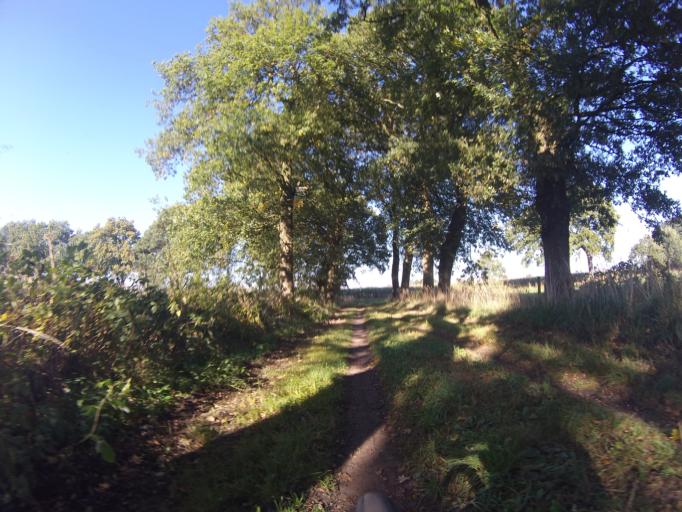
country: NL
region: Drenthe
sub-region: Gemeente Coevorden
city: Dalen
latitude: 52.7398
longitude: 6.6683
